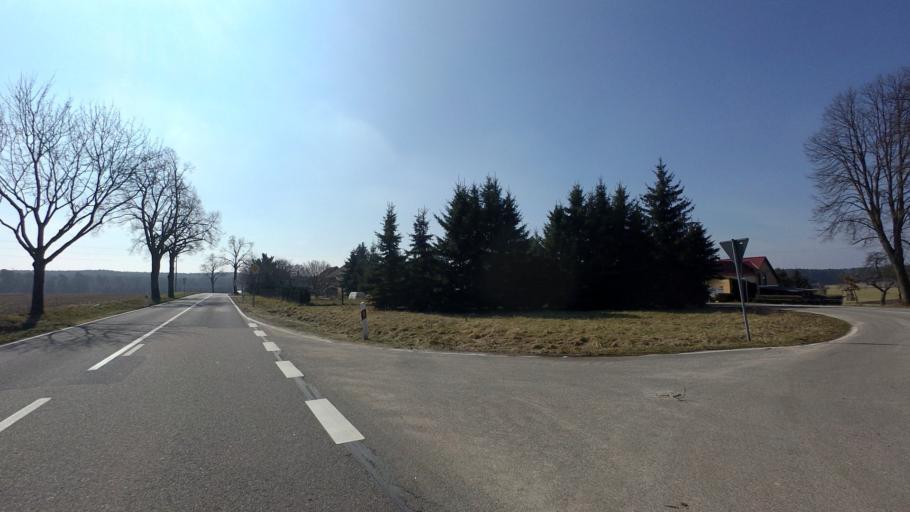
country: DE
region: Saxony-Anhalt
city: Nudersdorf
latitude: 51.9965
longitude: 12.5842
